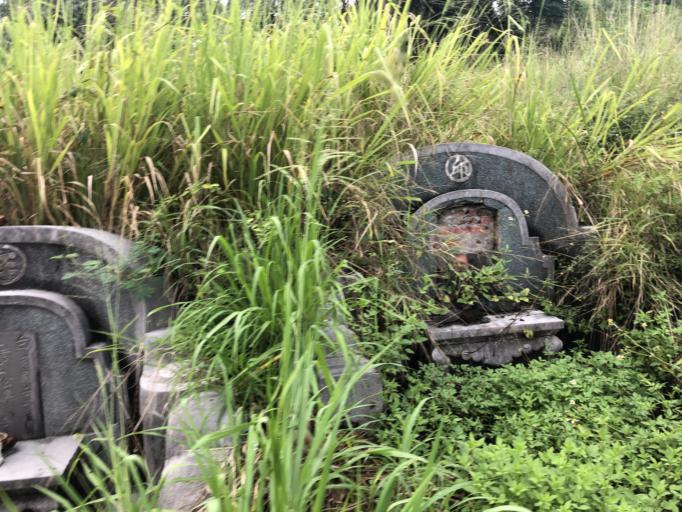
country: TW
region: Taiwan
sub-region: Tainan
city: Tainan
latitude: 22.9662
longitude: 120.1992
